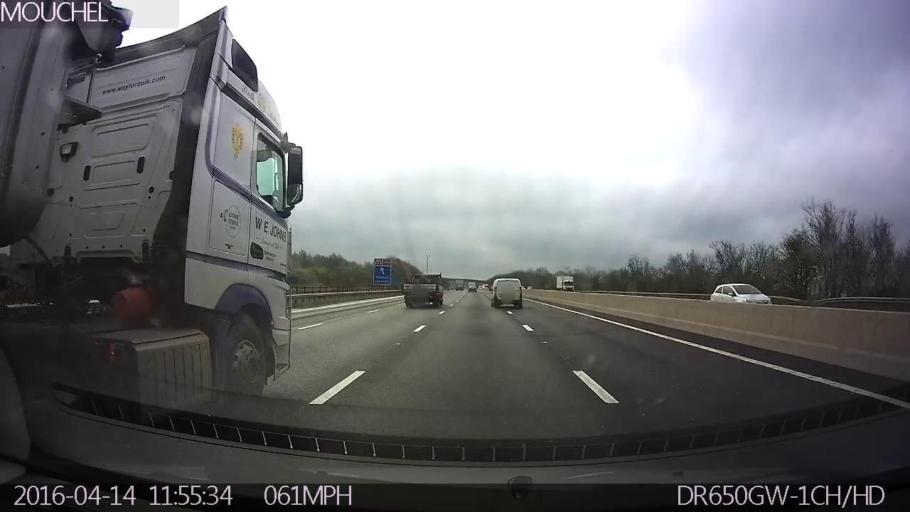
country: GB
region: England
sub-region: Derbyshire
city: Tibshelf
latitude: 53.1431
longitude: -1.3309
